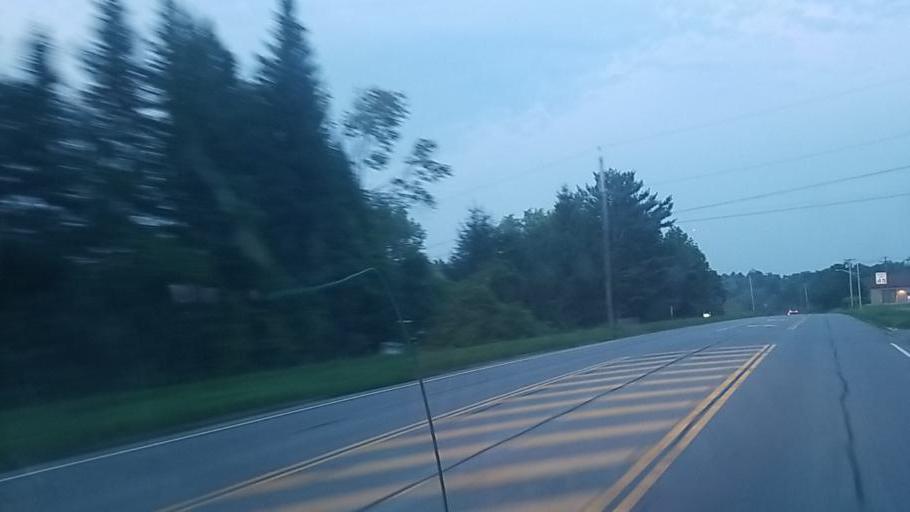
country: US
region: New York
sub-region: Fulton County
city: Johnstown
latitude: 42.9965
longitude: -74.3652
